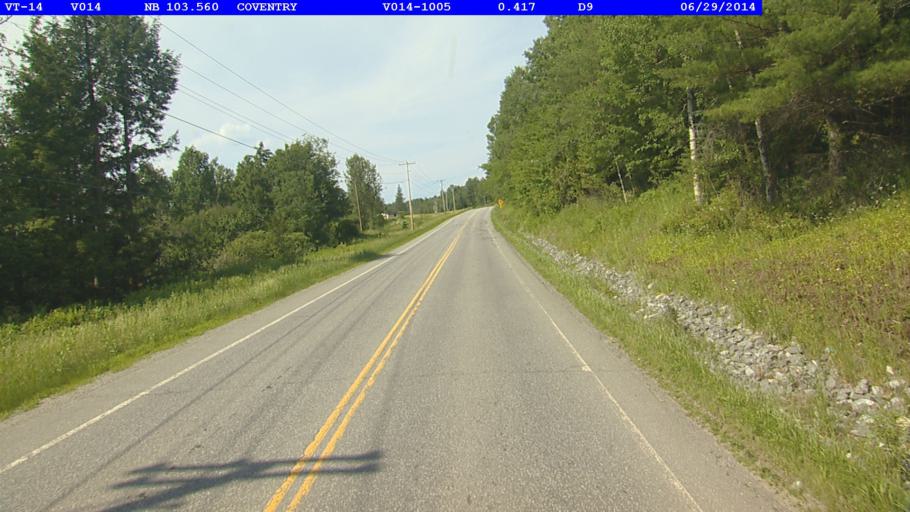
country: US
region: Vermont
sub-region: Orleans County
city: Newport
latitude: 44.8709
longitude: -72.2634
